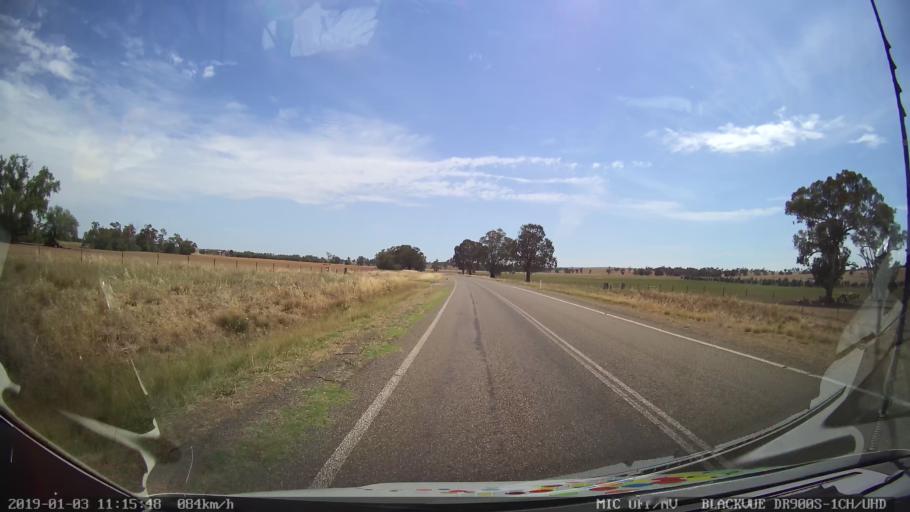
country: AU
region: New South Wales
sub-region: Young
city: Young
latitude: -34.1598
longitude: 148.2677
